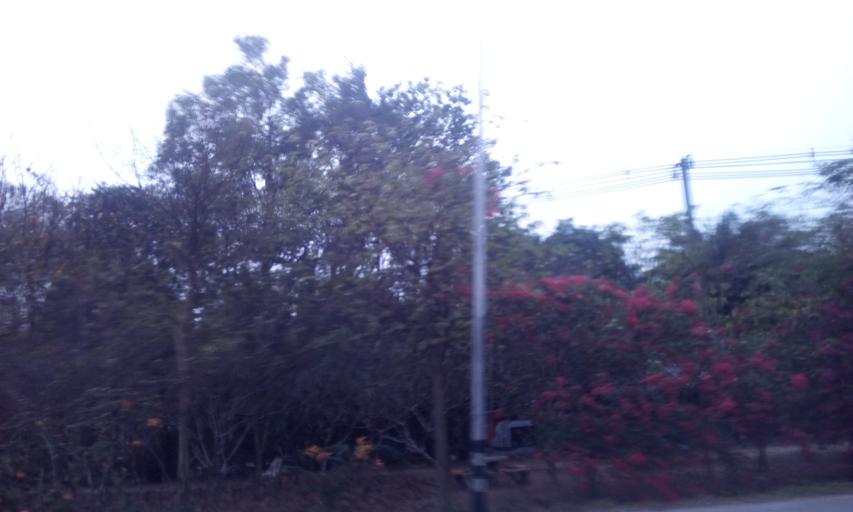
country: TH
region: Chon Buri
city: Ko Chan
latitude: 13.3314
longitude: 101.2703
